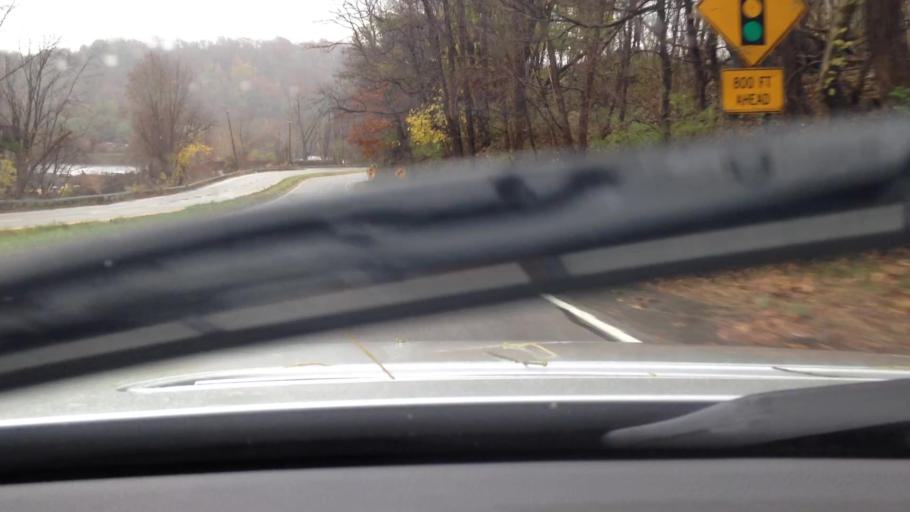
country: US
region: New York
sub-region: Westchester County
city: Peekskill
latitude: 41.3078
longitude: -73.9309
